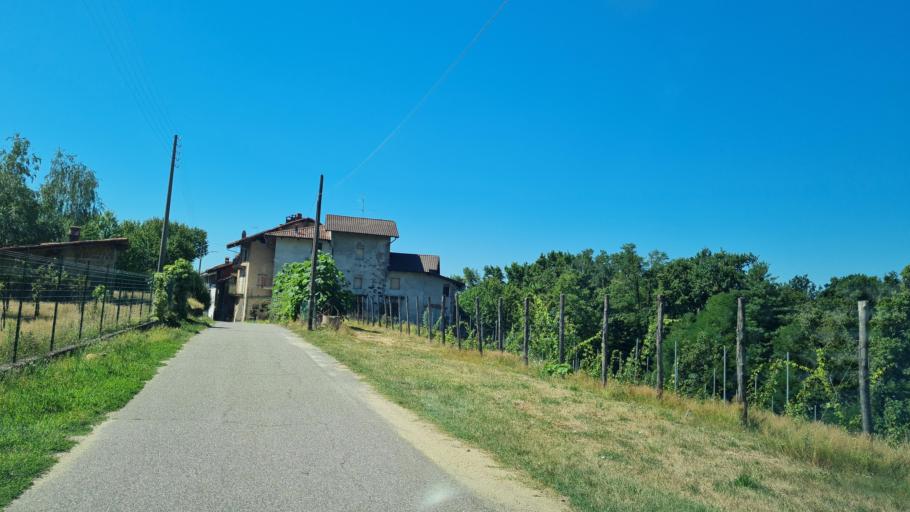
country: IT
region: Piedmont
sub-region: Provincia di Biella
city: Masserano
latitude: 45.5919
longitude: 8.2181
